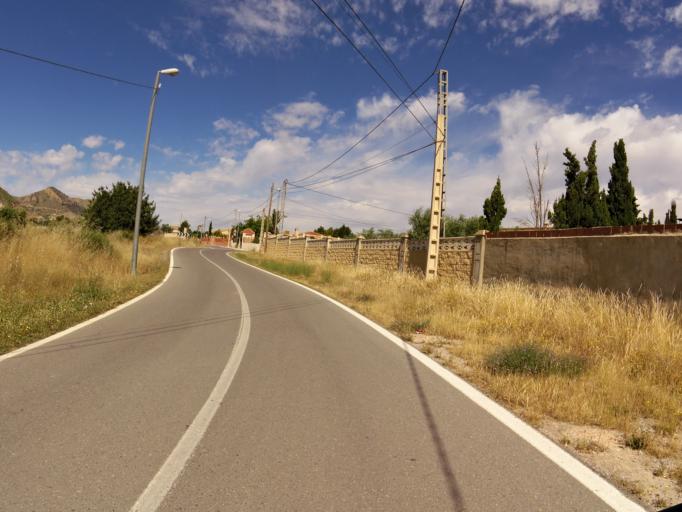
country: ES
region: Valencia
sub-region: Provincia de Alicante
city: Agost
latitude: 38.3957
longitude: -0.6007
